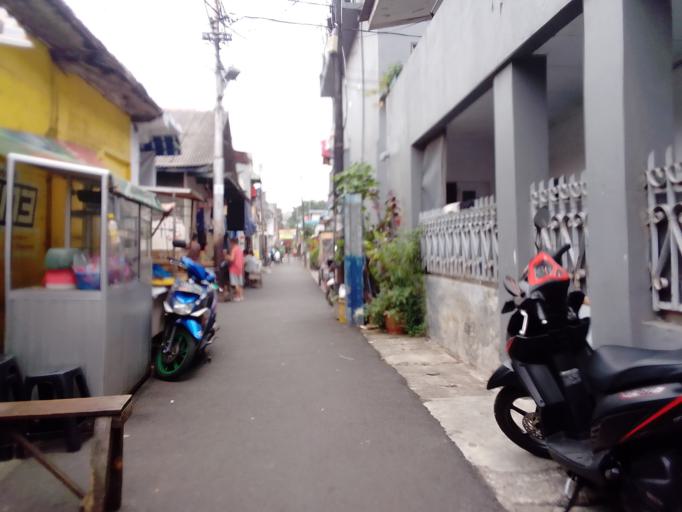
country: ID
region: Jakarta Raya
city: Jakarta
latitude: -6.1674
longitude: 106.8112
